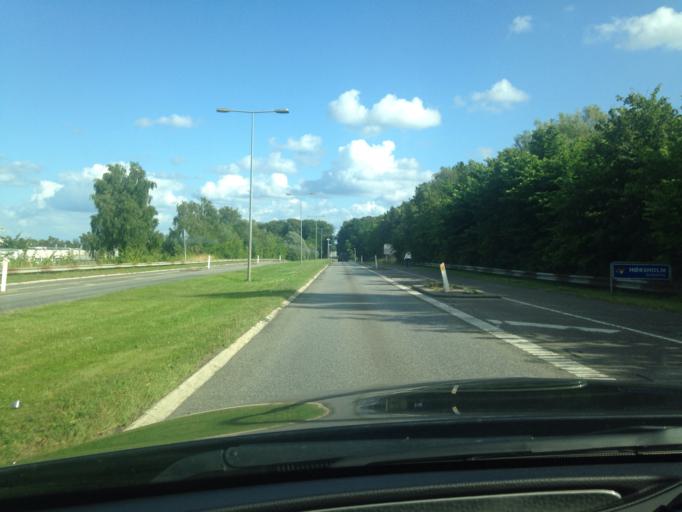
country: DK
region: Capital Region
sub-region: Fredensborg Kommune
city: Kokkedal
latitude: 55.9046
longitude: 12.4770
